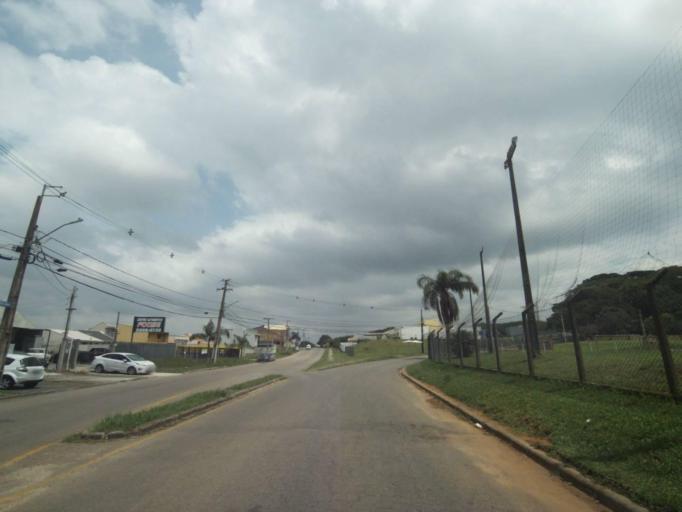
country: BR
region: Parana
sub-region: Curitiba
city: Curitiba
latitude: -25.4878
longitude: -49.3549
